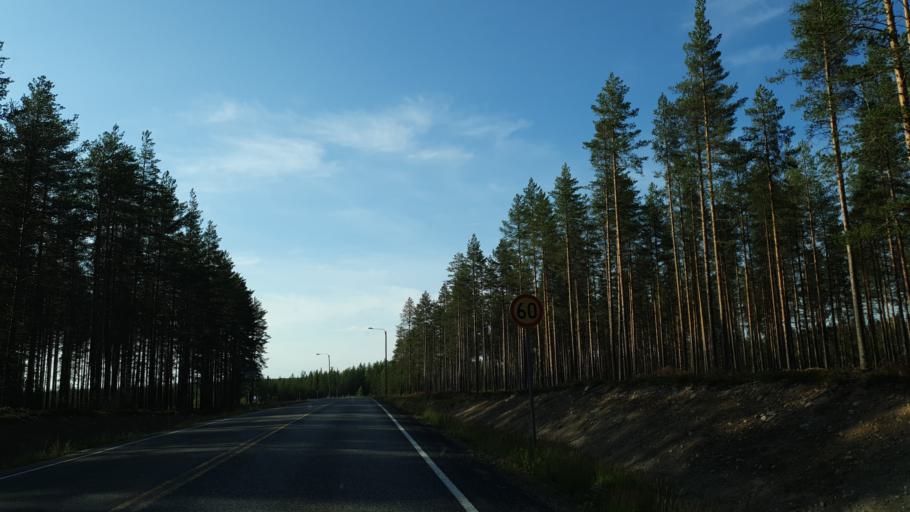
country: FI
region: Kainuu
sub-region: Kehys-Kainuu
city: Kuhmo
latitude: 64.0977
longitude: 29.4757
